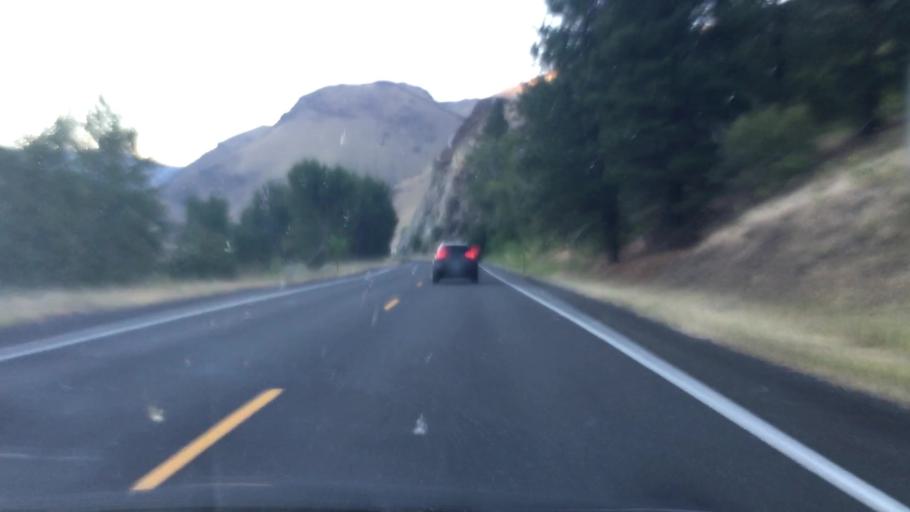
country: US
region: Idaho
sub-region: Valley County
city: McCall
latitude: 45.3278
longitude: -116.3474
